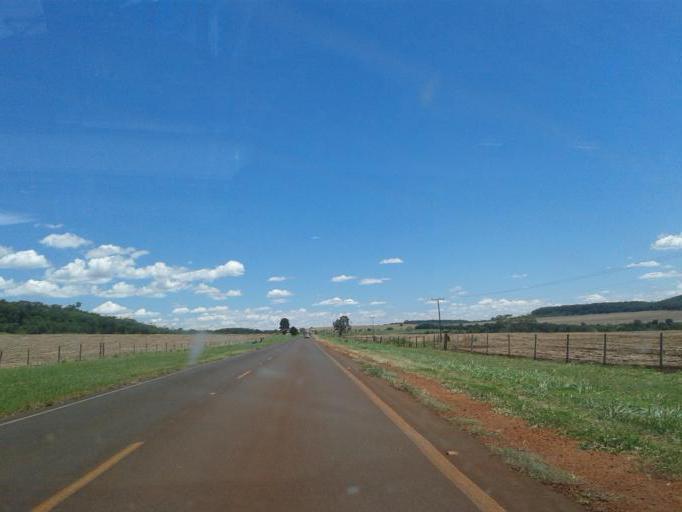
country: BR
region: Minas Gerais
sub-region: Capinopolis
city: Capinopolis
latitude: -18.6150
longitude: -49.5304
